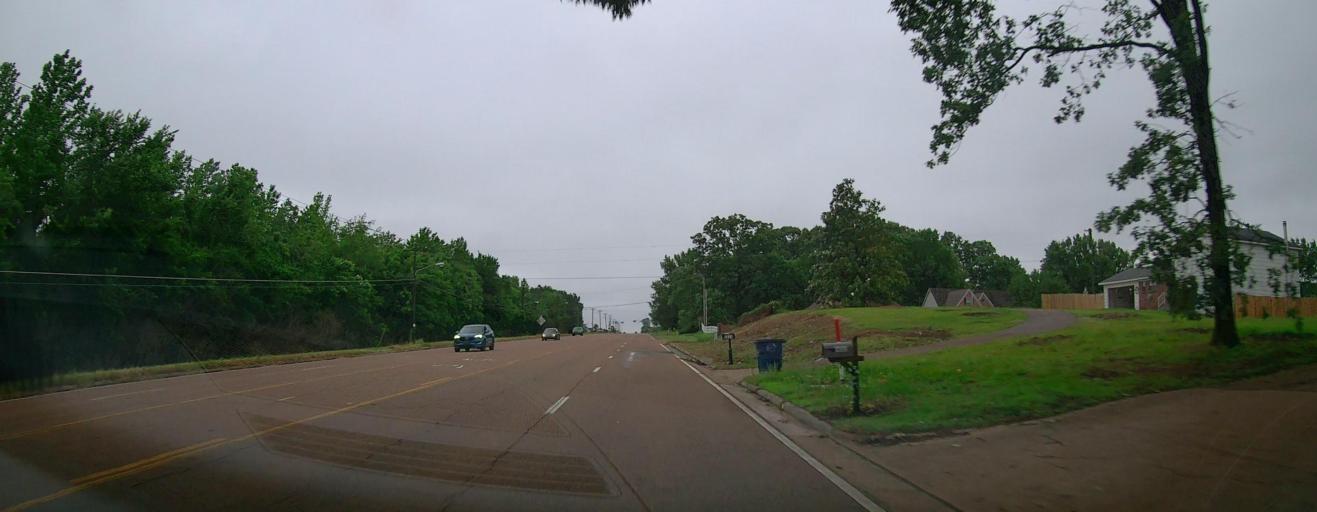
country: US
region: Mississippi
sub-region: De Soto County
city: Olive Branch
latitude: 34.9430
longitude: -89.7951
